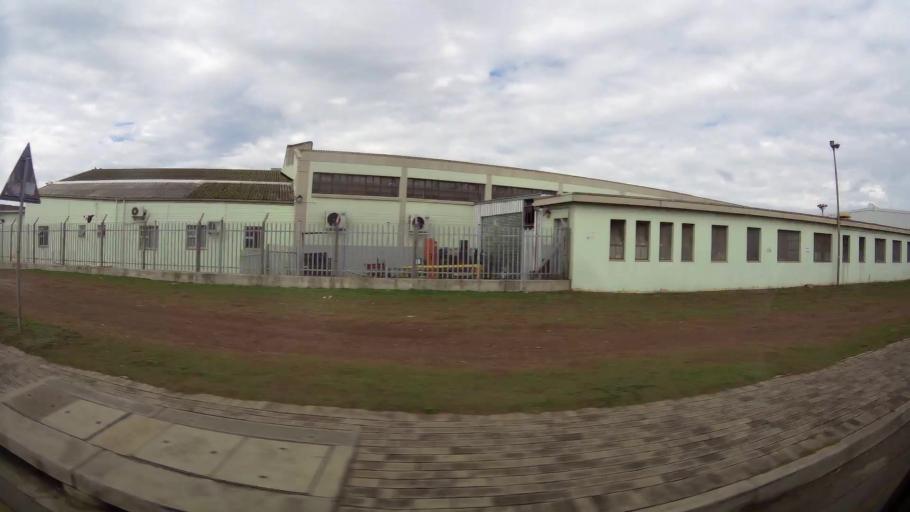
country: ZA
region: Eastern Cape
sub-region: Nelson Mandela Bay Metropolitan Municipality
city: Port Elizabeth
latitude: -33.9273
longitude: 25.5807
